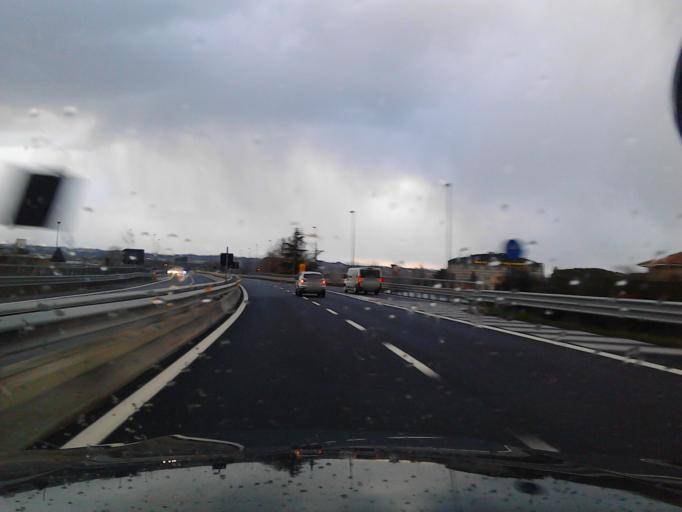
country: IT
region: Abruzzo
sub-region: Provincia di Pescara
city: Santa Teresa
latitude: 42.3981
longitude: 14.1672
